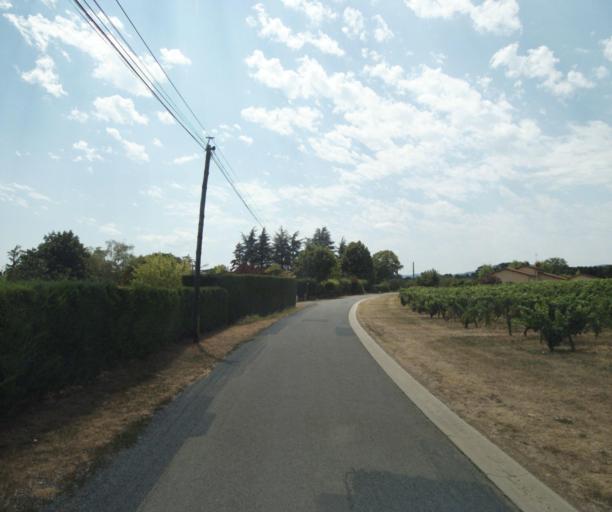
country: FR
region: Rhone-Alpes
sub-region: Departement du Rhone
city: Chatillon
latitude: 45.8685
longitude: 4.6215
